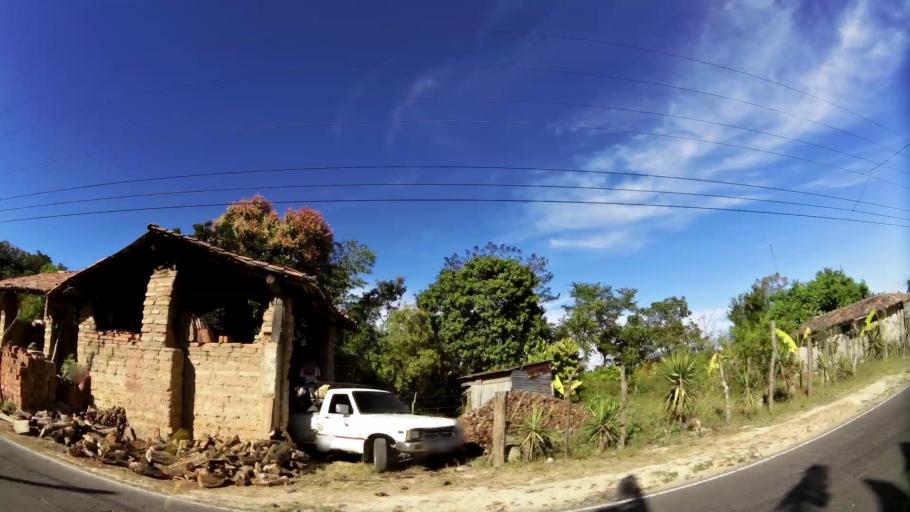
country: SV
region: Cuscatlan
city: Tenancingo
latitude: 13.8291
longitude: -89.0301
